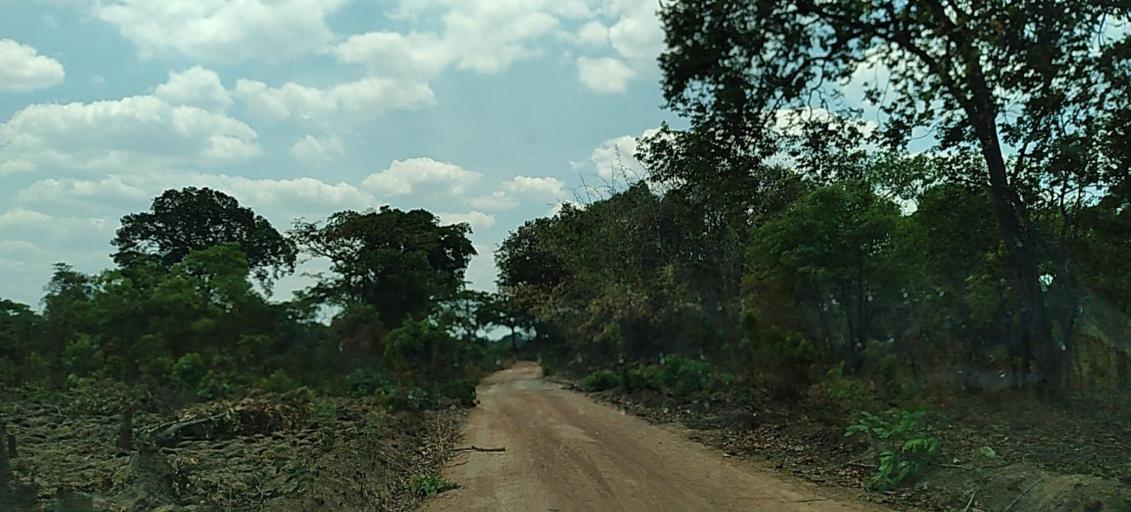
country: ZM
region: Copperbelt
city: Chililabombwe
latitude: -12.3924
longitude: 27.9211
